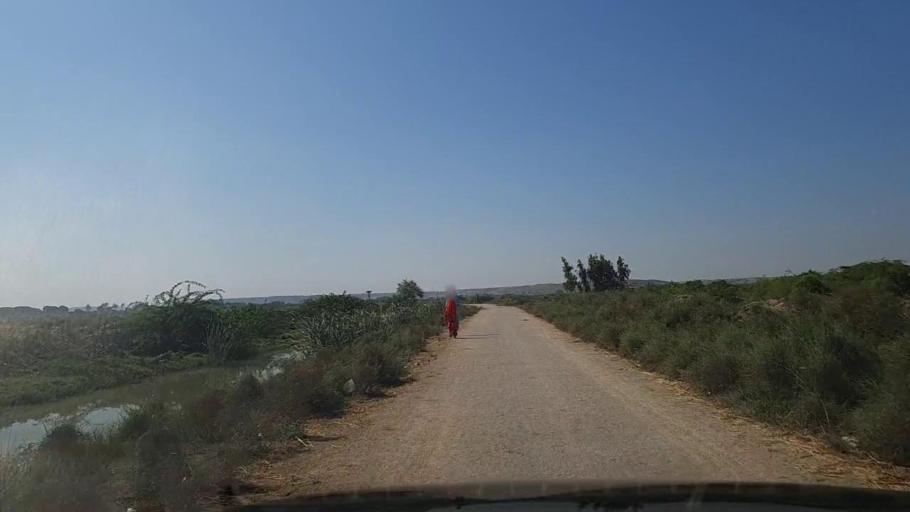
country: PK
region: Sindh
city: Thatta
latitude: 24.6331
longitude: 67.8726
